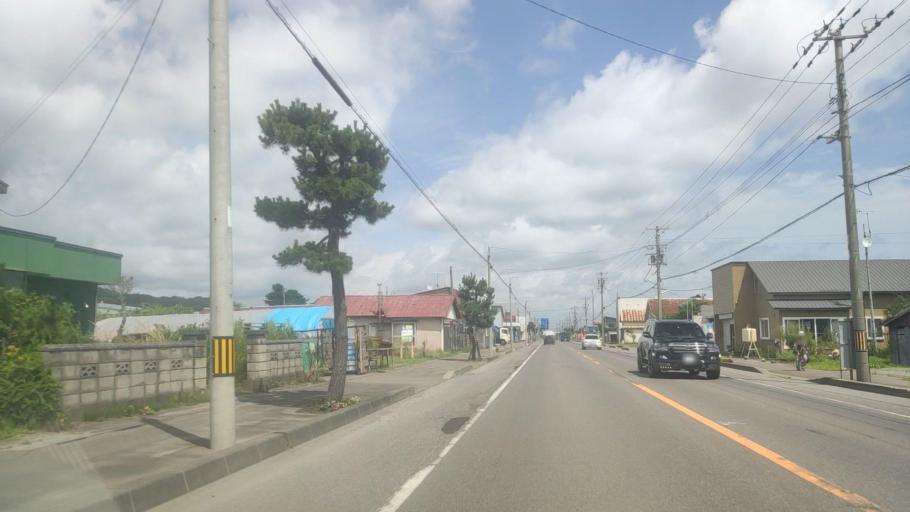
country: JP
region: Hokkaido
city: Niseko Town
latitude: 42.4361
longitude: 140.3217
